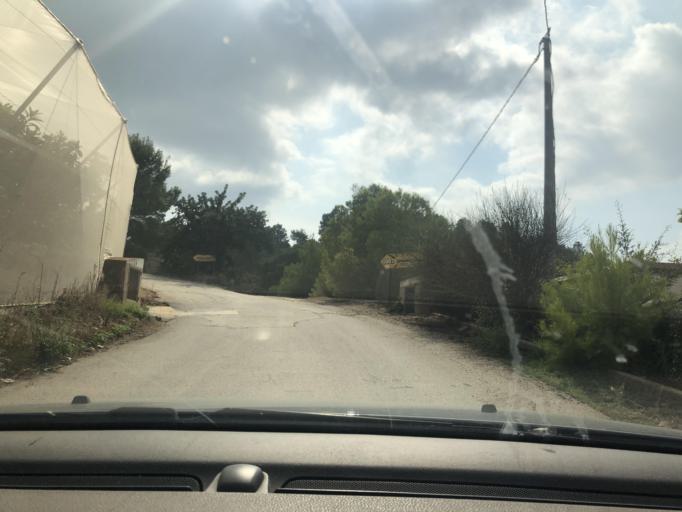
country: ES
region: Valencia
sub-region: Provincia de Alicante
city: Callosa d'En Sarria
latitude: 38.6544
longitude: -0.0925
